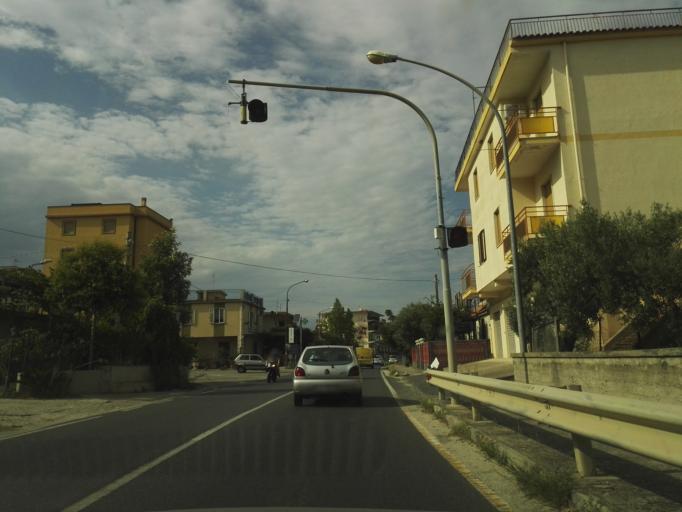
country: IT
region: Calabria
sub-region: Provincia di Catanzaro
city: Marina di Davoli
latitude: 38.6508
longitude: 16.5476
